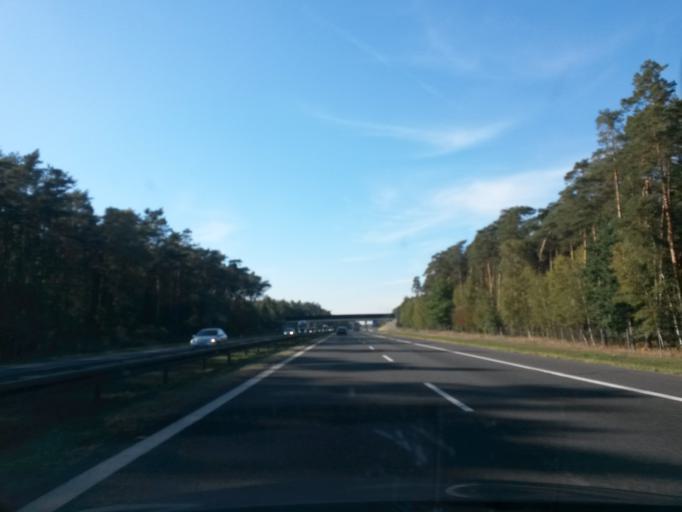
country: PL
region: Opole Voivodeship
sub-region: Powiat opolski
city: Niemodlin
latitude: 50.6698
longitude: 17.6708
